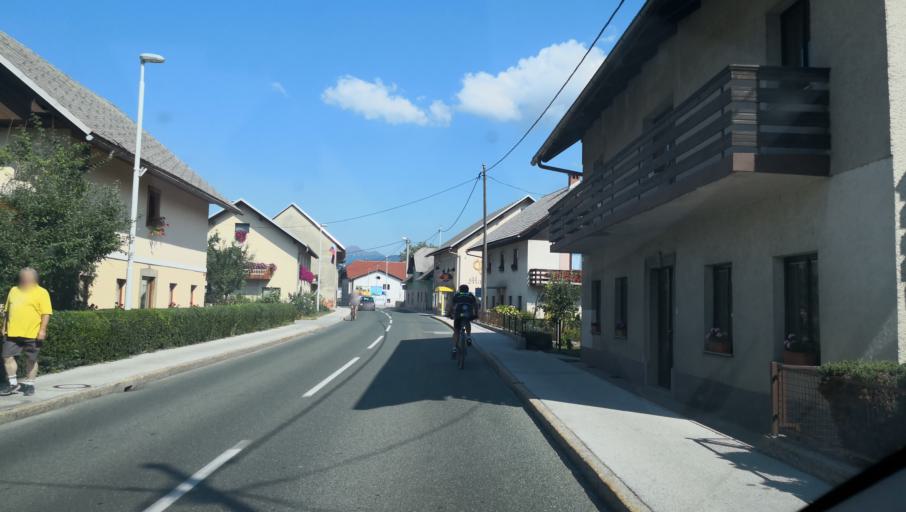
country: SI
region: Radovljica
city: Lesce
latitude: 46.3590
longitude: 14.1622
